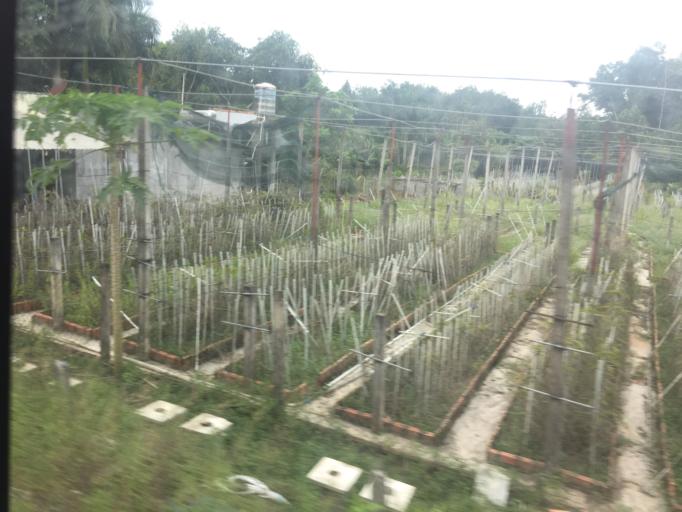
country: VN
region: Ho Chi Minh City
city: Cu Chi
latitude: 11.1214
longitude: 106.4790
